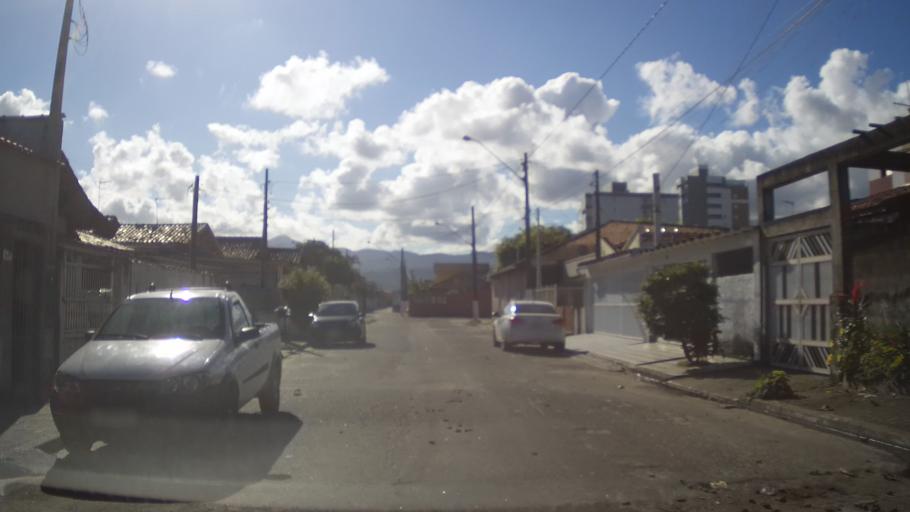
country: BR
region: Sao Paulo
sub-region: Praia Grande
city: Praia Grande
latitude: -24.0324
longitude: -46.4858
